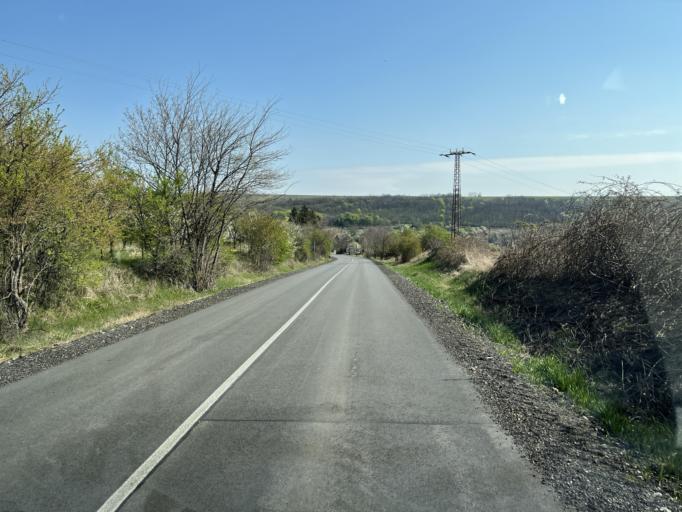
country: HU
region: Pest
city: Orbottyan
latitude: 47.7334
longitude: 19.2864
